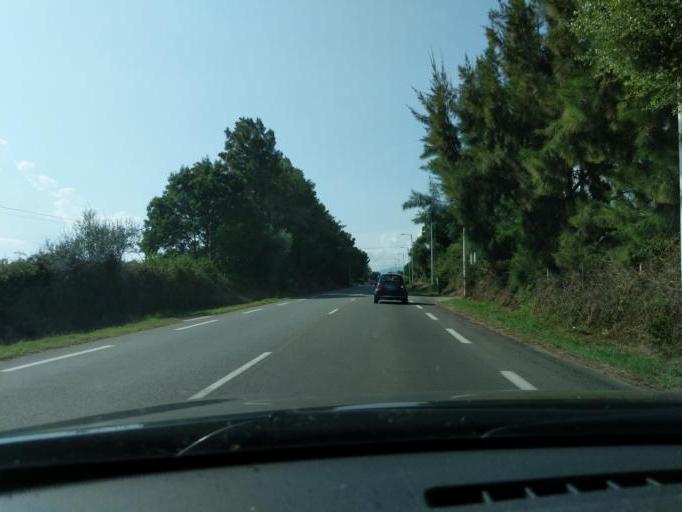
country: FR
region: Corsica
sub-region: Departement de la Haute-Corse
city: Ghisonaccia
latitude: 41.9607
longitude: 9.3968
